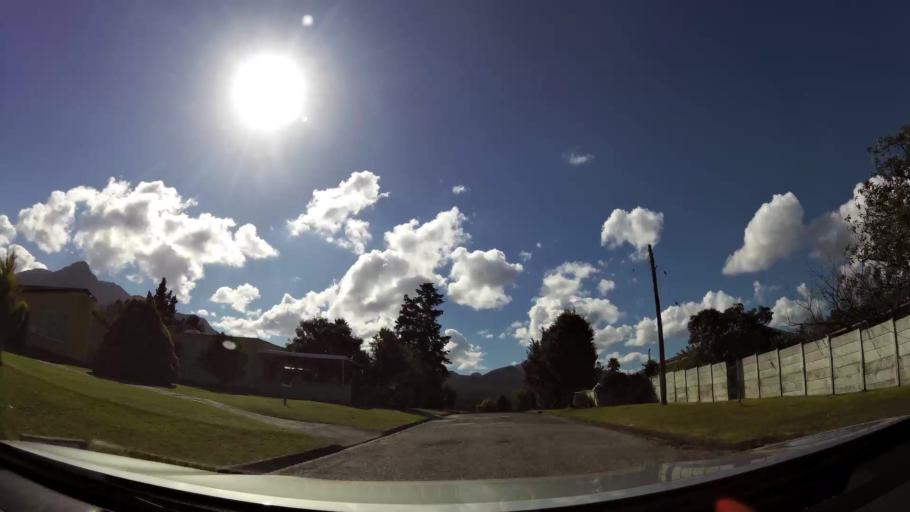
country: ZA
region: Western Cape
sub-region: Eden District Municipality
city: George
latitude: -33.9541
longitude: 22.4807
